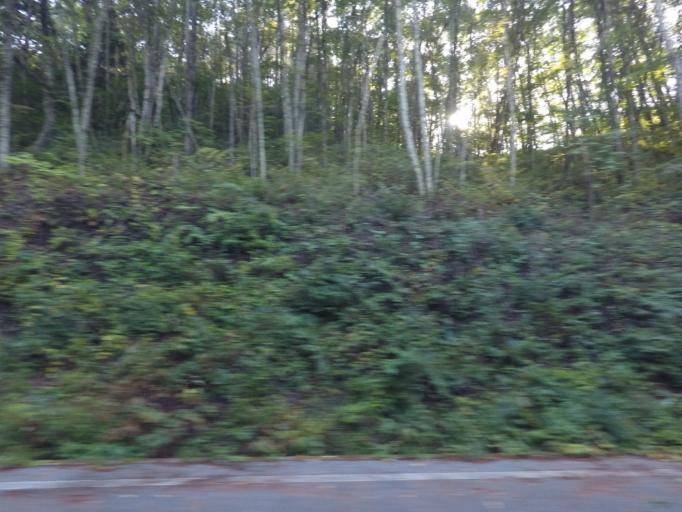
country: JP
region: Nagano
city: Tatsuno
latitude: 35.9639
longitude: 137.7749
